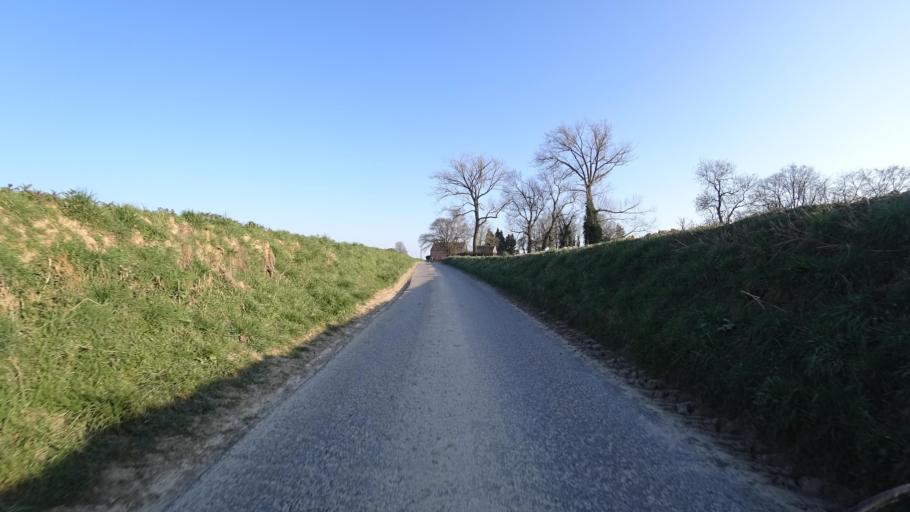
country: BE
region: Wallonia
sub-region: Province du Brabant Wallon
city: Chastre
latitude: 50.5839
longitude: 4.6479
